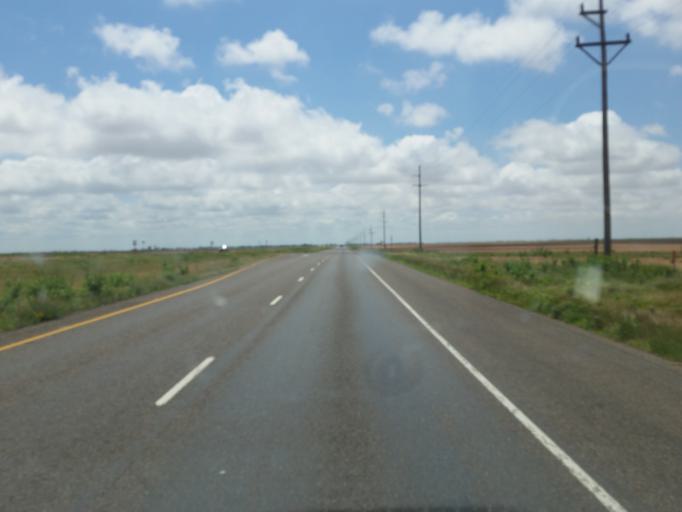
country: US
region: Texas
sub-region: Lubbock County
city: Slaton
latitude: 33.3897
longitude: -101.5983
